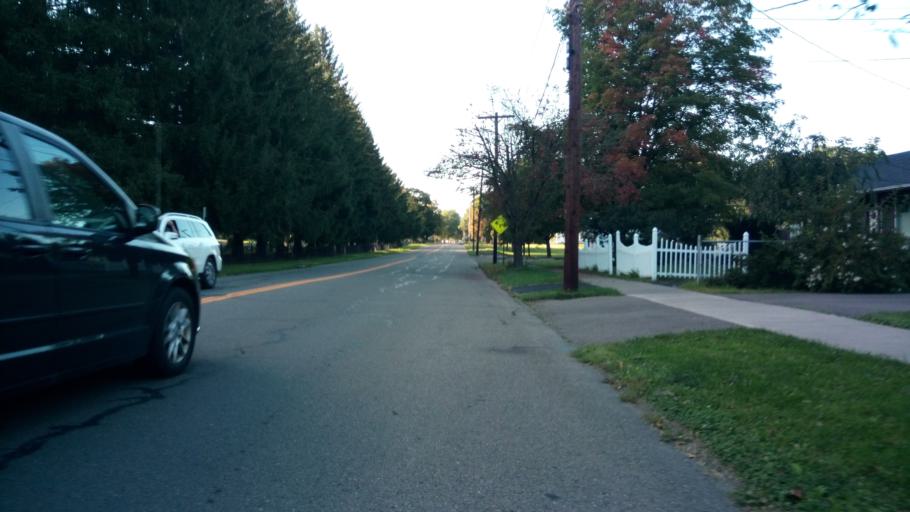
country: US
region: New York
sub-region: Chemung County
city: Elmira
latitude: 42.1062
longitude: -76.8239
